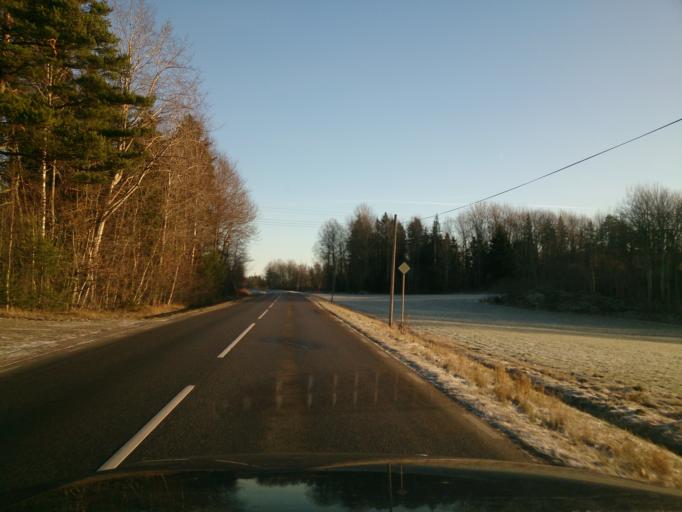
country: SE
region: OEstergoetland
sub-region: Norrkopings Kommun
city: Kimstad
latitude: 58.3908
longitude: 15.9731
